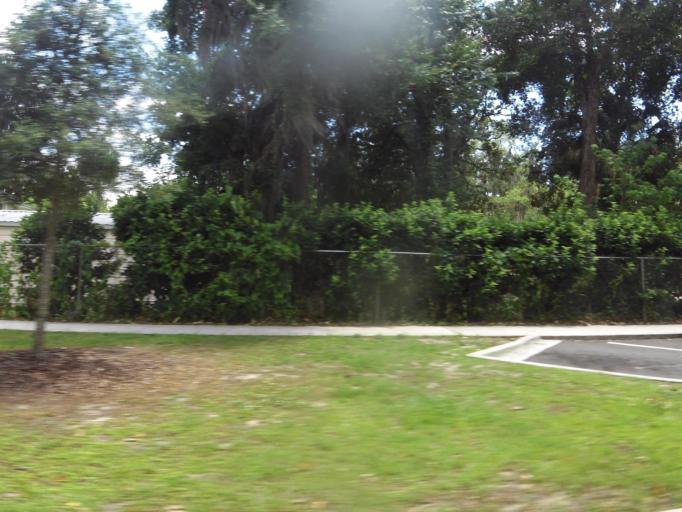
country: US
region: Florida
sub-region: Clay County
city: Orange Park
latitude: 30.1660
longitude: -81.6963
